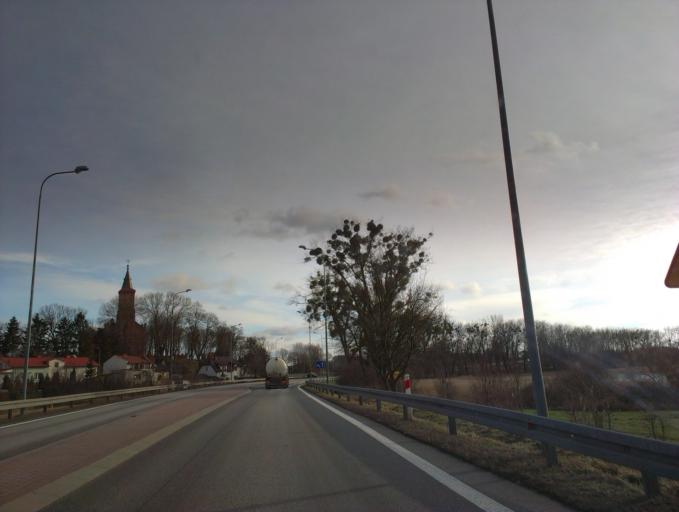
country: PL
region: Kujawsko-Pomorskie
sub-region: Powiat lipnowski
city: Kikol
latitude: 52.9108
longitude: 19.1179
